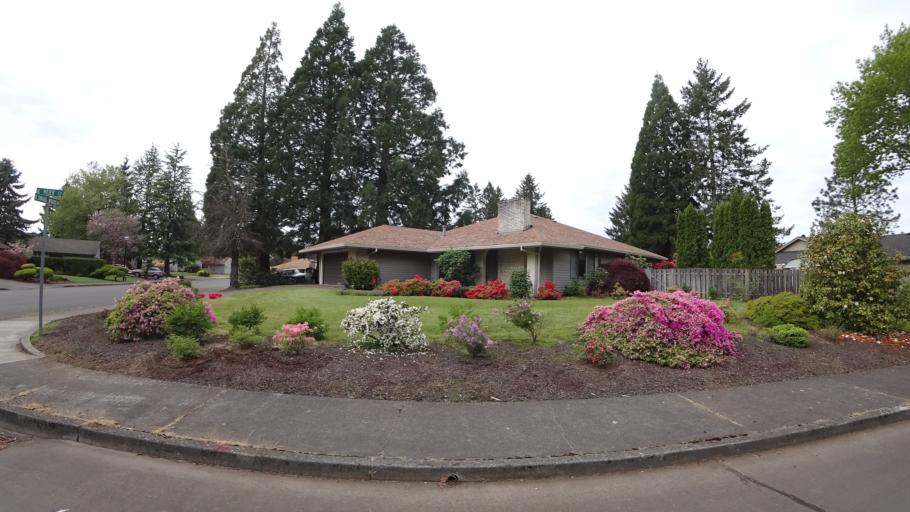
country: US
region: Oregon
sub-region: Washington County
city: Hillsboro
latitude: 45.4913
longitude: -122.9592
